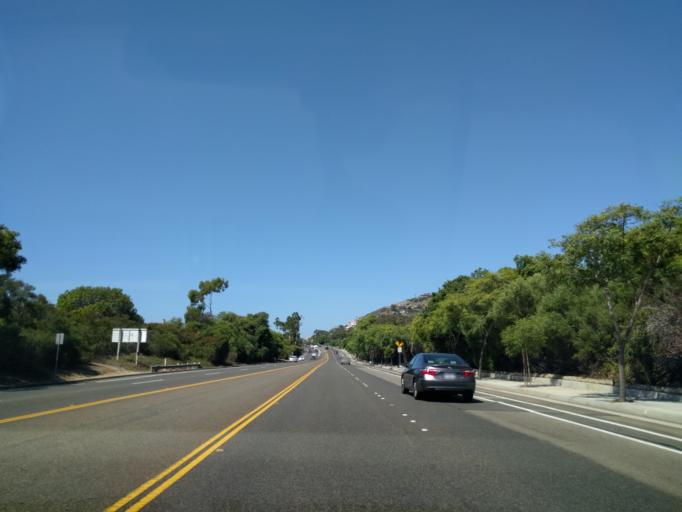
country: US
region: California
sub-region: Orange County
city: Dana Point
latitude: 33.4880
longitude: -117.7285
